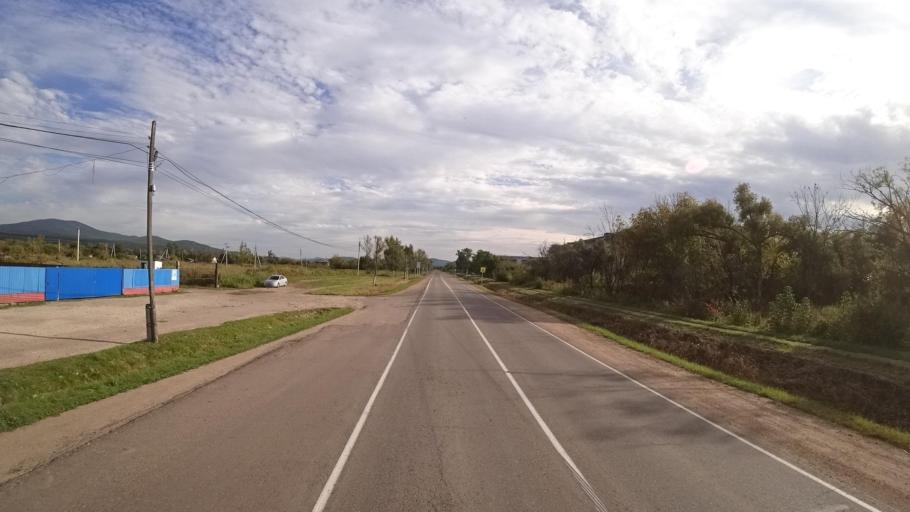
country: RU
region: Primorskiy
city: Dostoyevka
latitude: 44.2928
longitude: 133.4265
